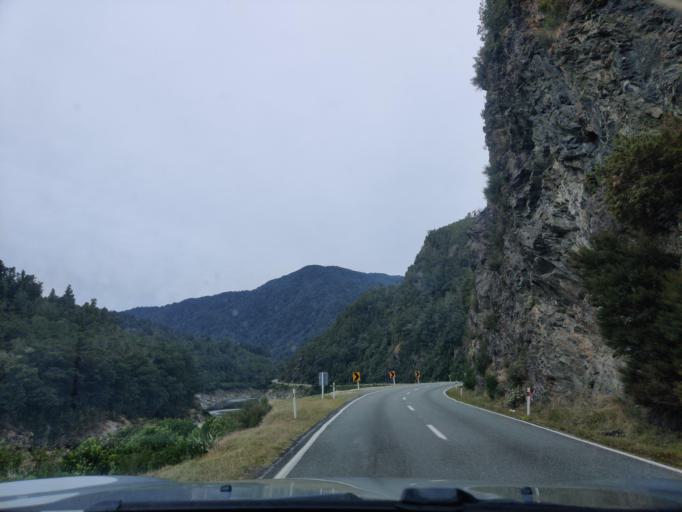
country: NZ
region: West Coast
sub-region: Buller District
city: Westport
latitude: -41.8493
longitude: 171.7327
